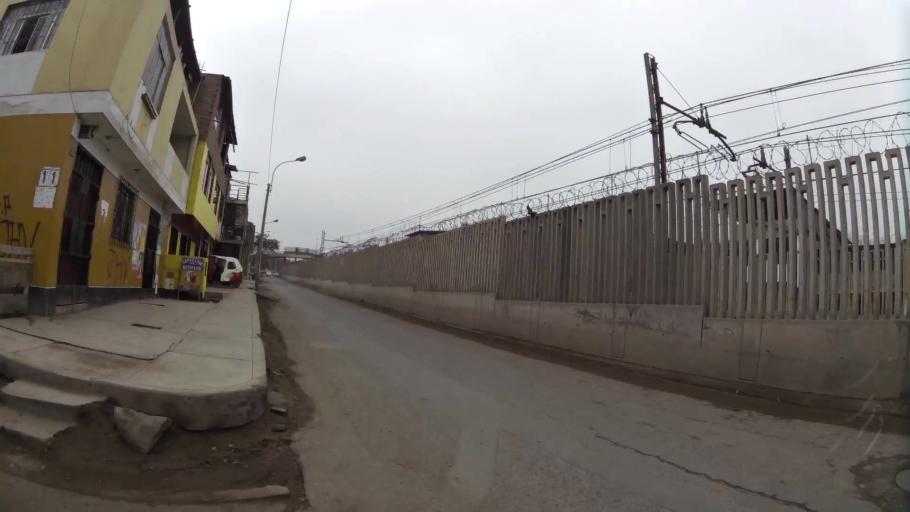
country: PE
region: Lima
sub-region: Lima
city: Surco
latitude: -12.1775
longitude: -76.9485
